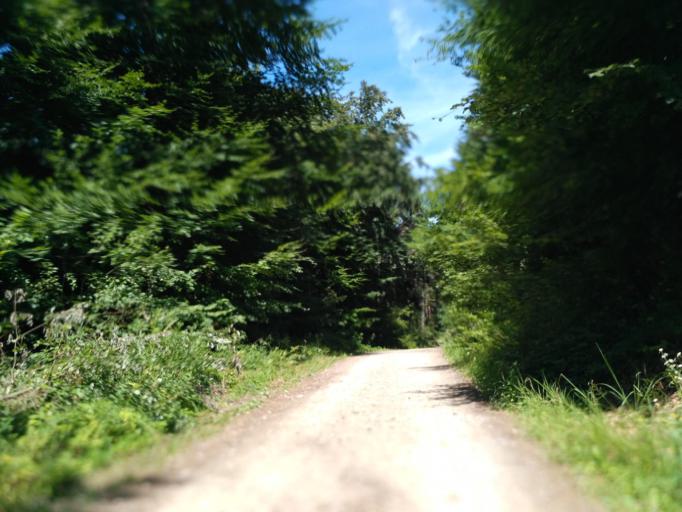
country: PL
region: Subcarpathian Voivodeship
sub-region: Powiat sanocki
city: Bukowsko
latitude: 49.4837
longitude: 22.0932
